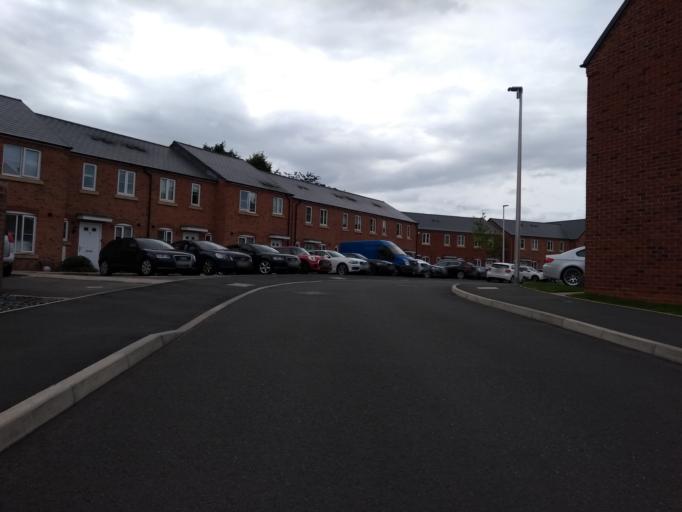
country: GB
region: England
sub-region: Warwickshire
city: Warwick
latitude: 52.2920
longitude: -1.5941
